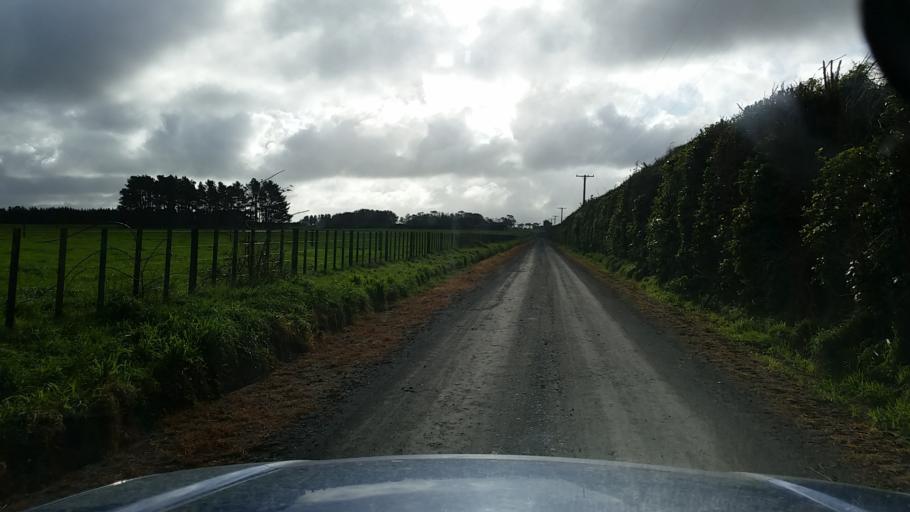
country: NZ
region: Taranaki
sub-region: South Taranaki District
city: Hawera
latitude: -39.5178
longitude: 174.3288
